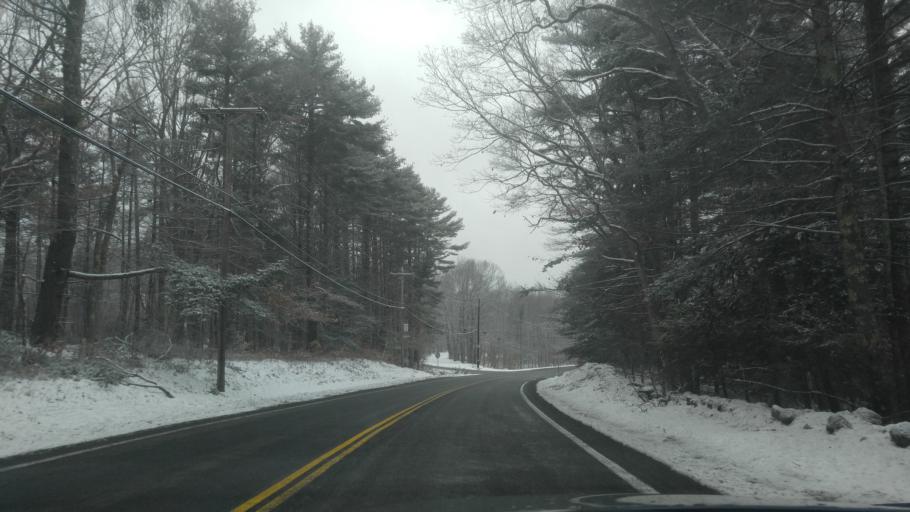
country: US
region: Rhode Island
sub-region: Providence County
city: Foster
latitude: 41.8282
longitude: -71.7504
